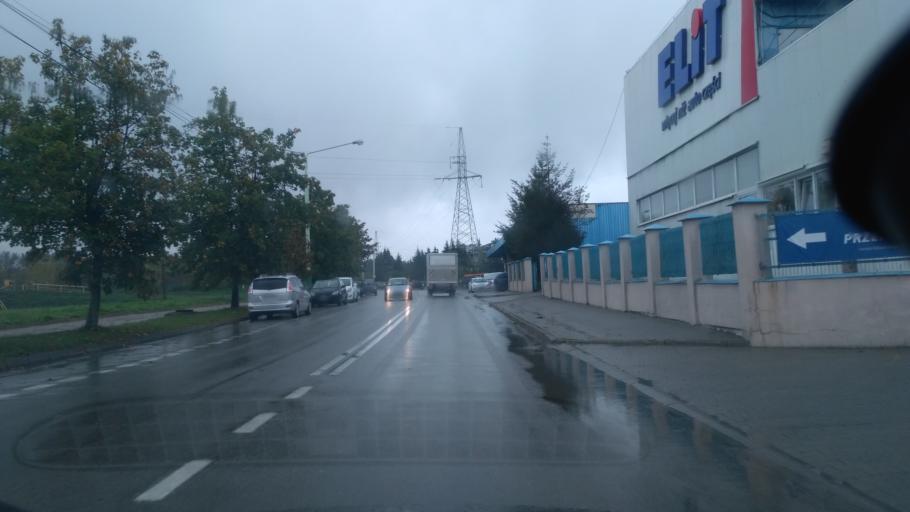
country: PL
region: Subcarpathian Voivodeship
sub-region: Powiat debicki
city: Debica
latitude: 50.0563
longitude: 21.3919
